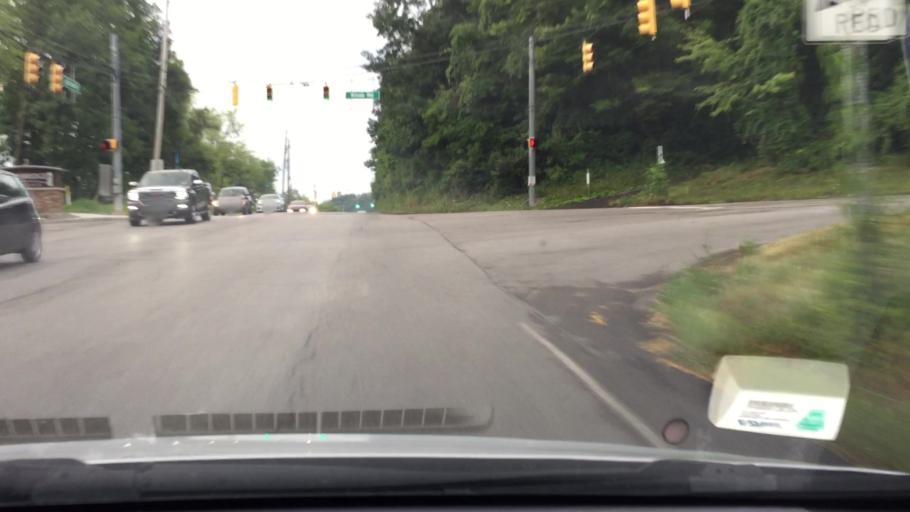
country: US
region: Pennsylvania
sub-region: Butler County
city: Cranberry Township
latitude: 40.6618
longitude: -80.0993
